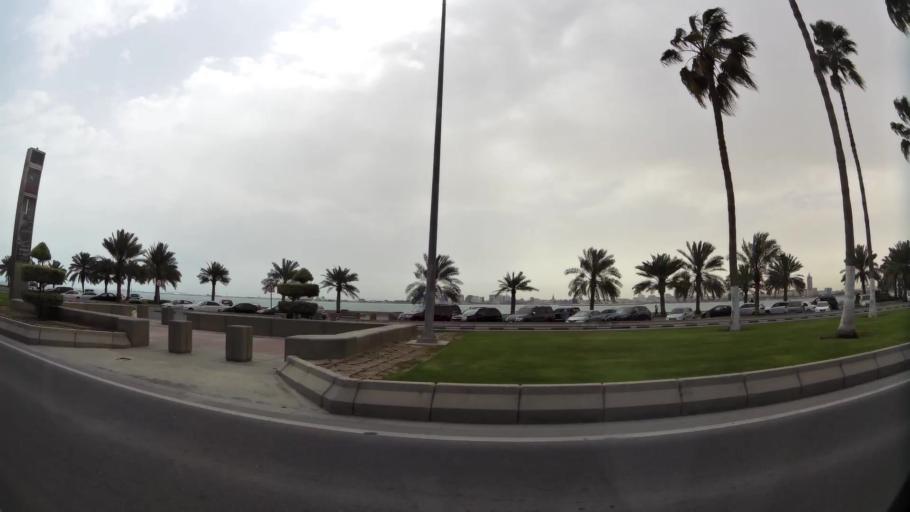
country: QA
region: Baladiyat ad Dawhah
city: Doha
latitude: 25.3153
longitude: 51.5248
